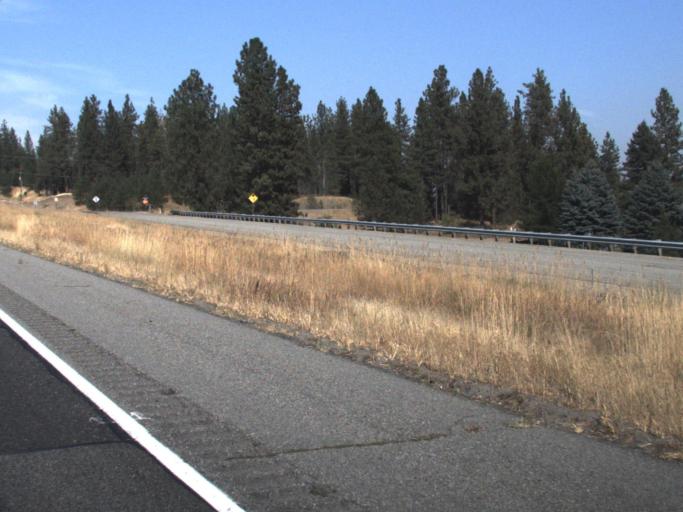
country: US
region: Washington
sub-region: Spokane County
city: Mead
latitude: 47.8944
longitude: -117.3526
